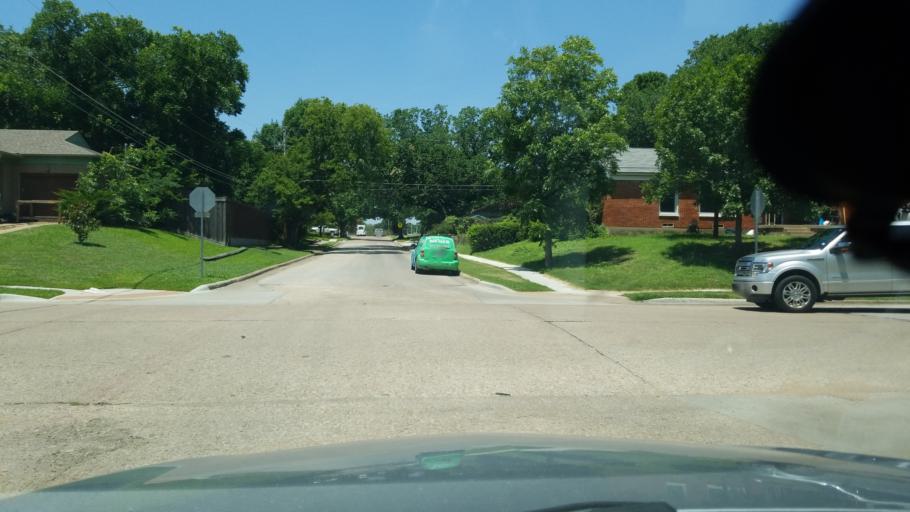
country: US
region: Texas
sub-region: Dallas County
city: Irving
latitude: 32.8343
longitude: -96.9736
